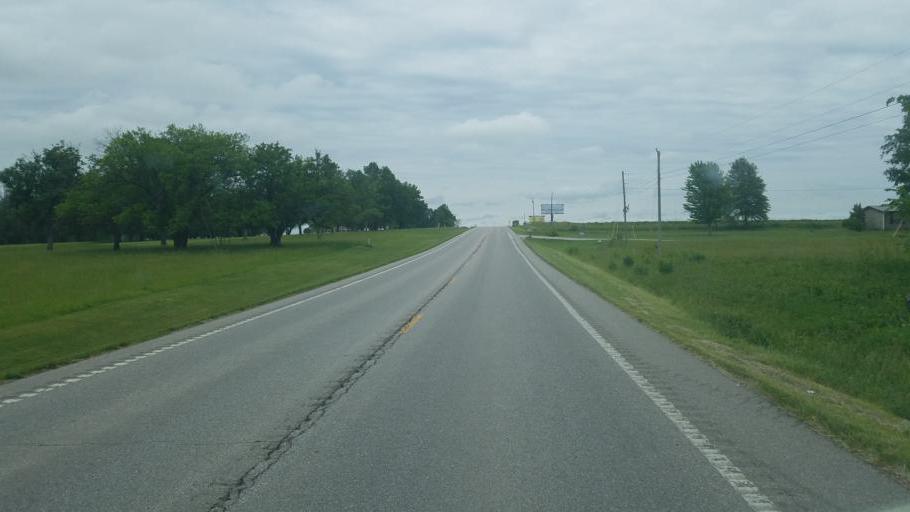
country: US
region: Missouri
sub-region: Morgan County
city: Versailles
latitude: 38.4664
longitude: -92.8089
